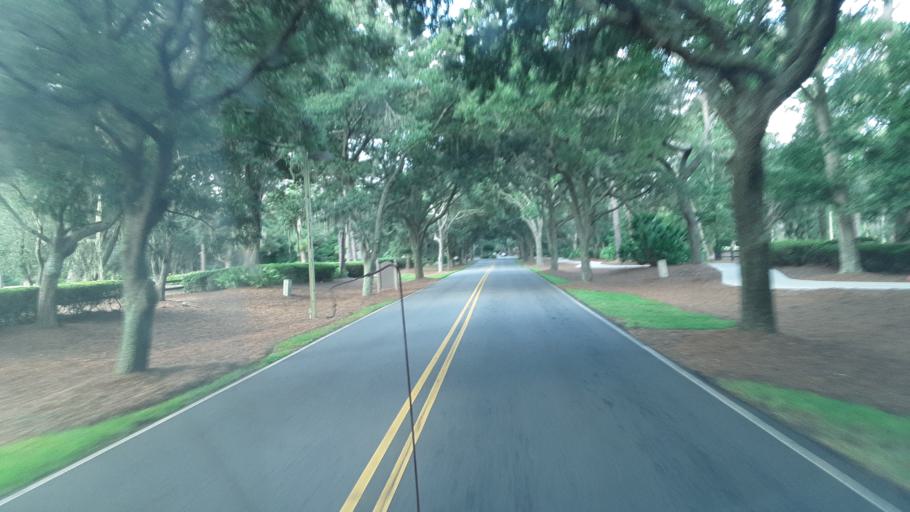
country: US
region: South Carolina
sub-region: Beaufort County
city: Hilton Head Island
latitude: 32.2124
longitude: -80.6899
